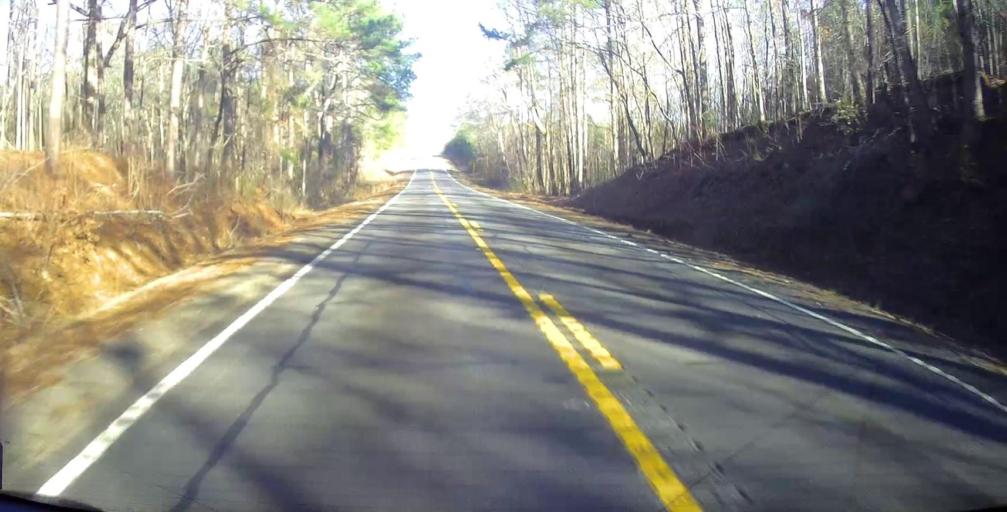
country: US
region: Georgia
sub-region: Talbot County
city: Talbotton
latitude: 32.6725
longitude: -84.5035
